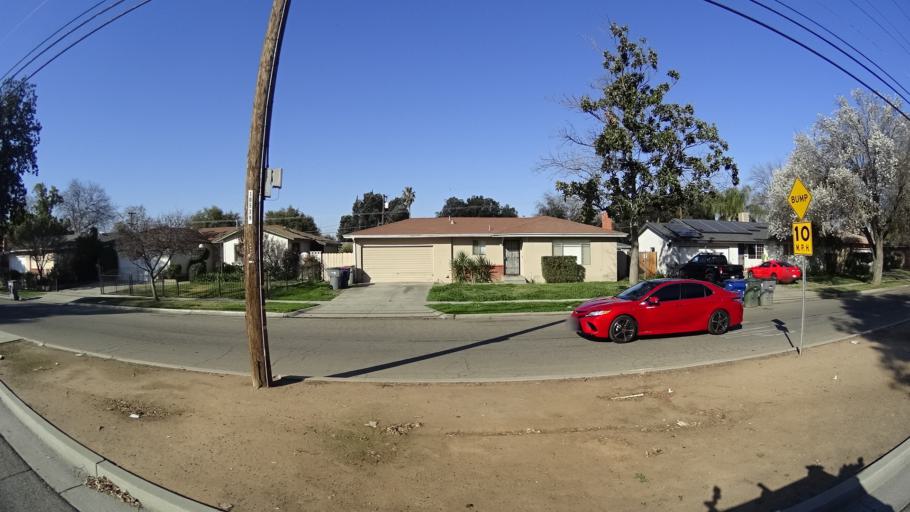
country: US
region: California
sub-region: Fresno County
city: Fresno
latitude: 36.7224
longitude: -119.7366
